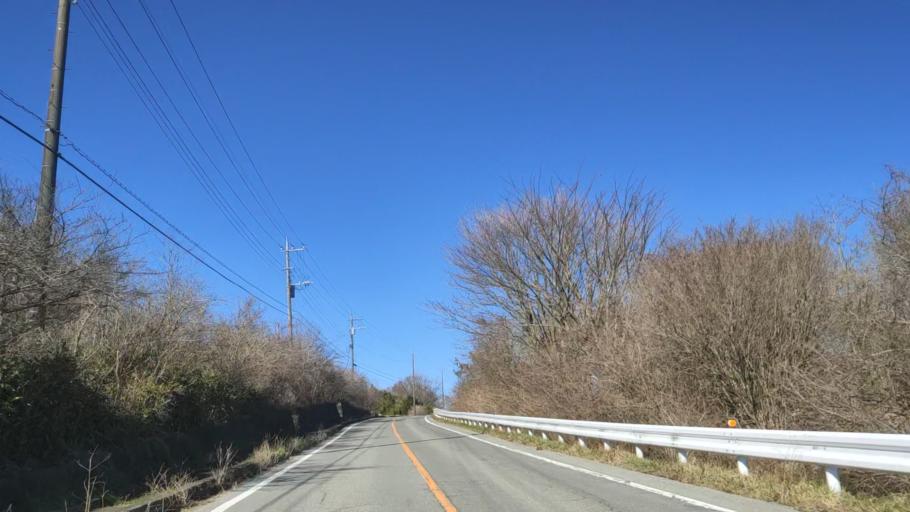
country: JP
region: Yamanashi
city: Fujikawaguchiko
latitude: 35.4103
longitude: 138.6182
